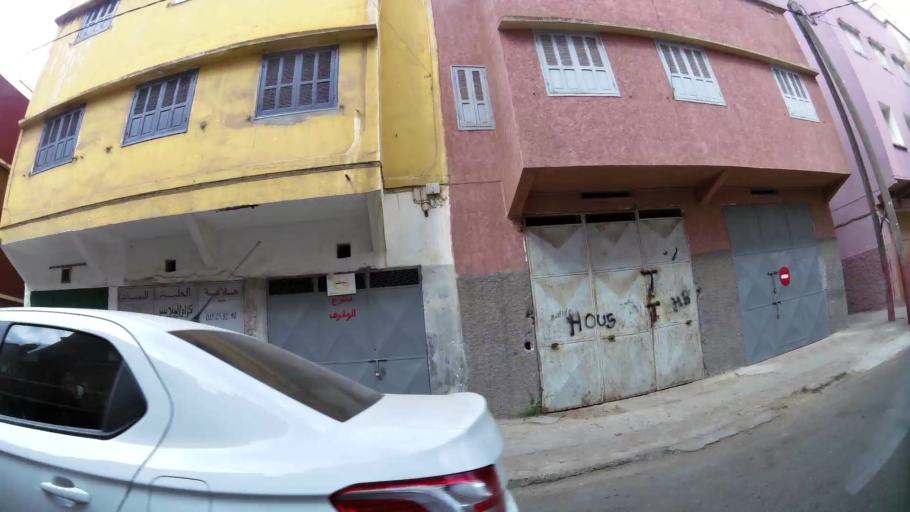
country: MA
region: Gharb-Chrarda-Beni Hssen
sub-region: Kenitra Province
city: Kenitra
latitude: 34.2600
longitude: -6.5685
